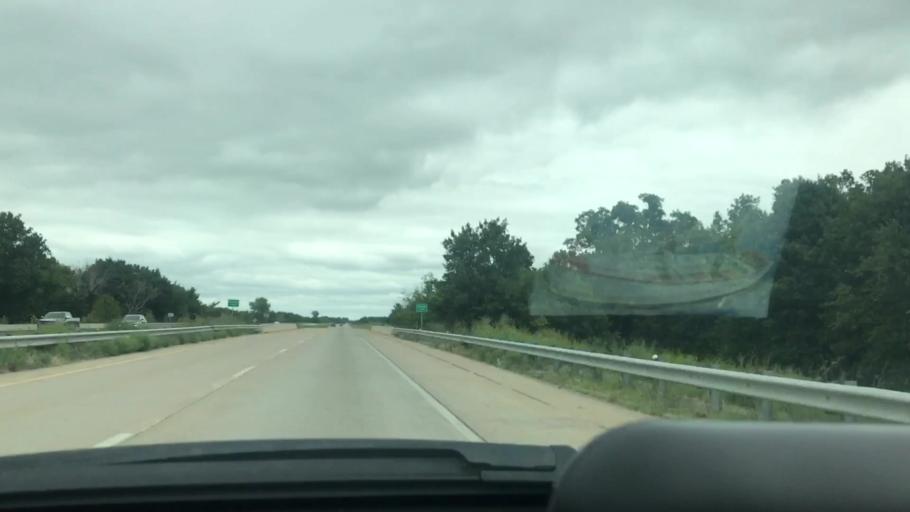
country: US
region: Oklahoma
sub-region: Mayes County
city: Chouteau
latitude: 36.2060
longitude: -95.3408
